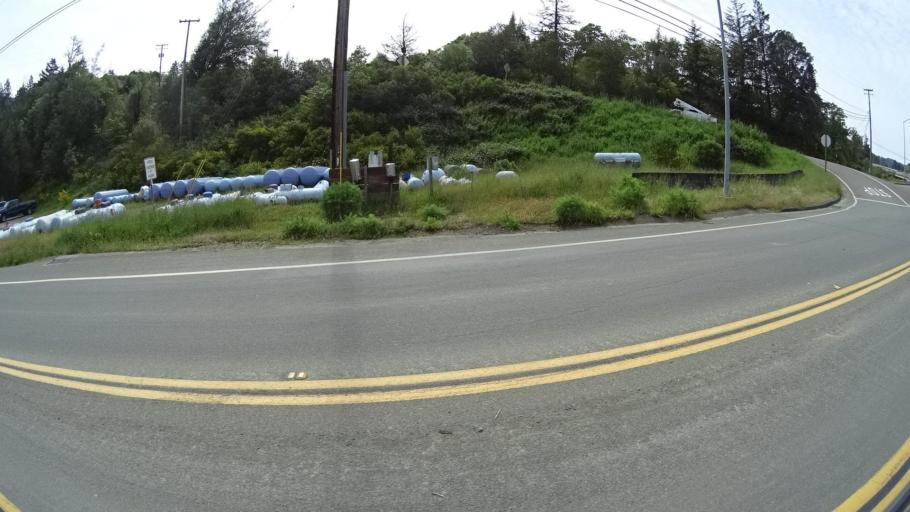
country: US
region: California
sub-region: Humboldt County
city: Redway
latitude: 40.1086
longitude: -123.7957
